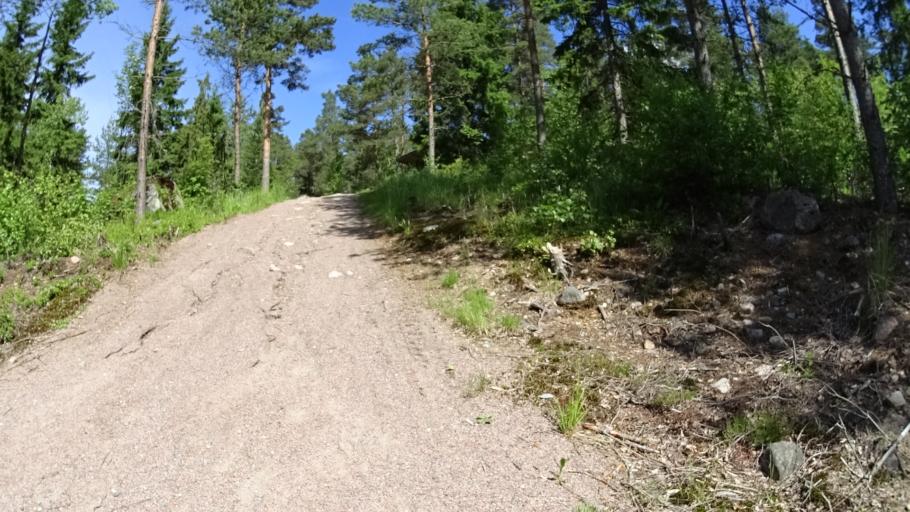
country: FI
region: Uusimaa
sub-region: Helsinki
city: Kilo
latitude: 60.3149
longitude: 24.7842
